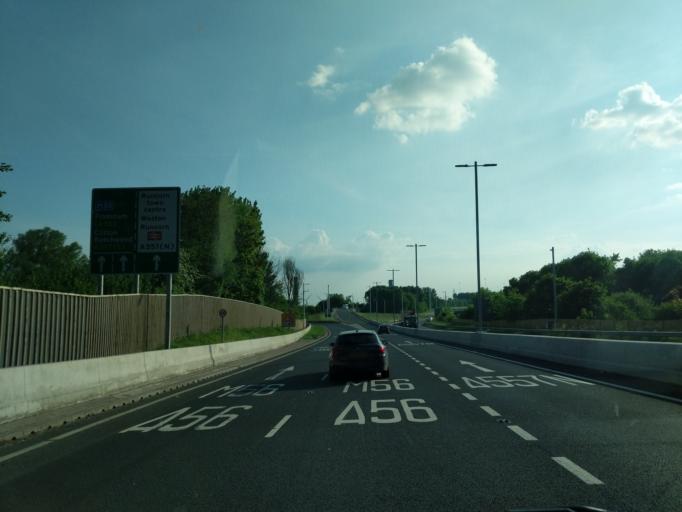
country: GB
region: England
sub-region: Borough of Halton
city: Halton
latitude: 53.3206
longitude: -2.7130
